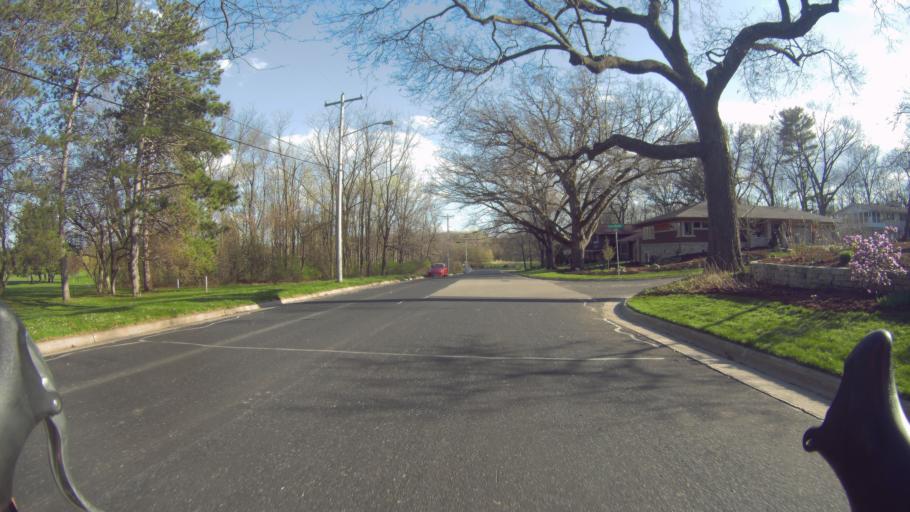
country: US
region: Wisconsin
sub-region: Dane County
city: Shorewood Hills
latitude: 43.0492
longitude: -89.4638
